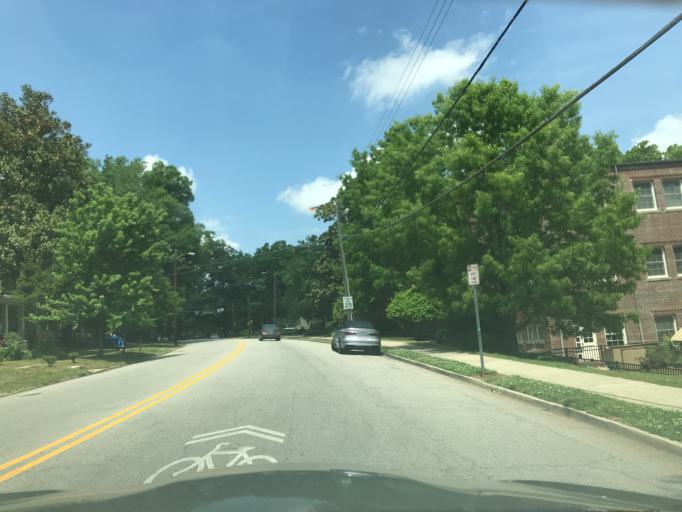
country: US
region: North Carolina
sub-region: Wake County
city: Raleigh
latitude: 35.7734
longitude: -78.6506
